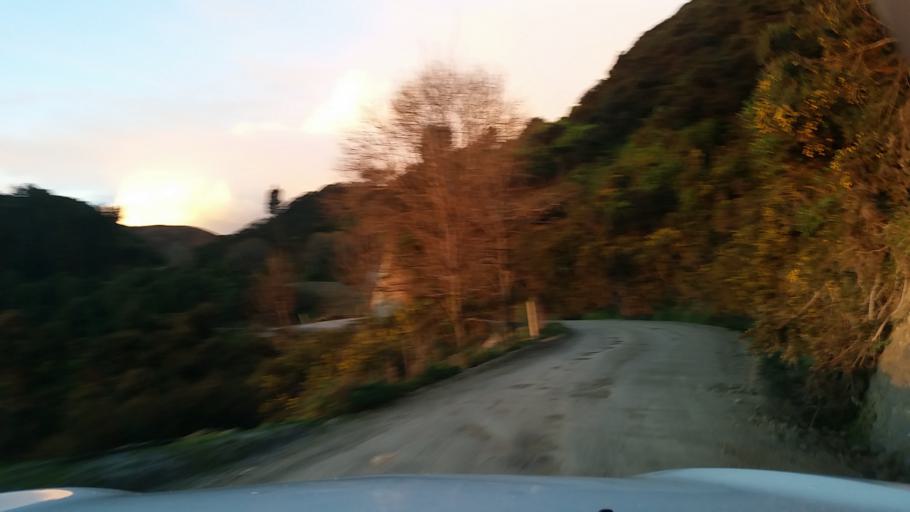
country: NZ
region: Manawatu-Wanganui
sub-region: Wanganui District
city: Wanganui
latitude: -39.7592
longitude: 174.8830
